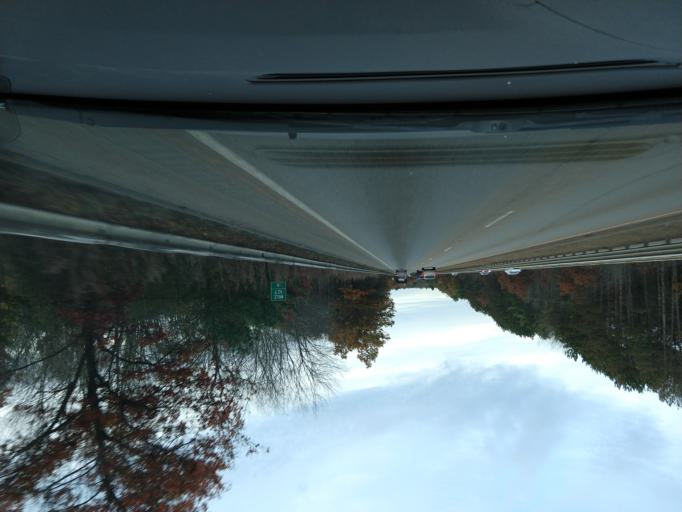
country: US
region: Massachusetts
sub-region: Worcester County
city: Harvard
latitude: 42.5178
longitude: -71.6134
